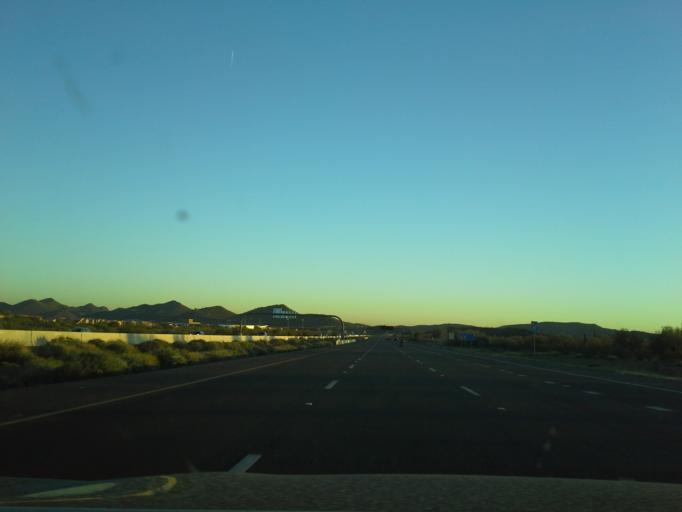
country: US
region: Arizona
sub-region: Maricopa County
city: Anthem
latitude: 33.8632
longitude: -112.1454
